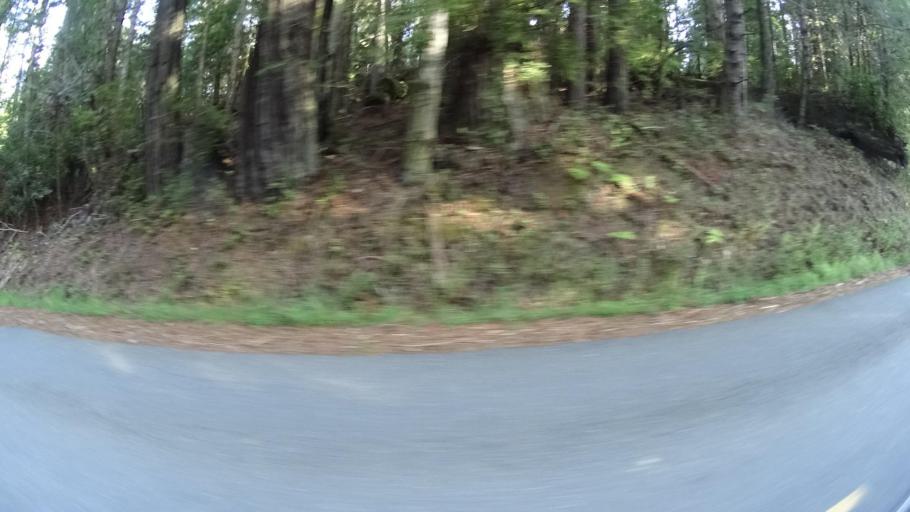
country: US
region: California
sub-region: Humboldt County
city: Bayside
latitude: 40.7594
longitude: -124.0178
